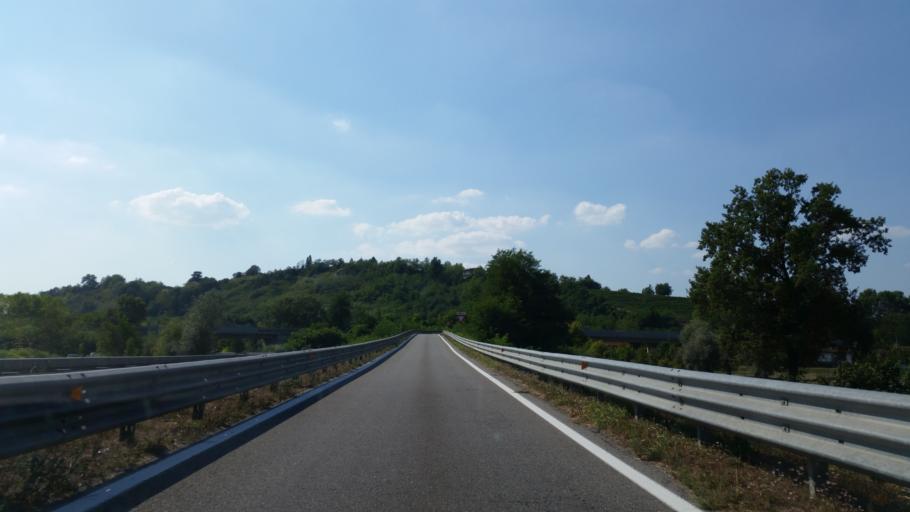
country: IT
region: Piedmont
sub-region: Provincia di Cuneo
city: Mussotto
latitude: 44.7106
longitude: 8.0154
